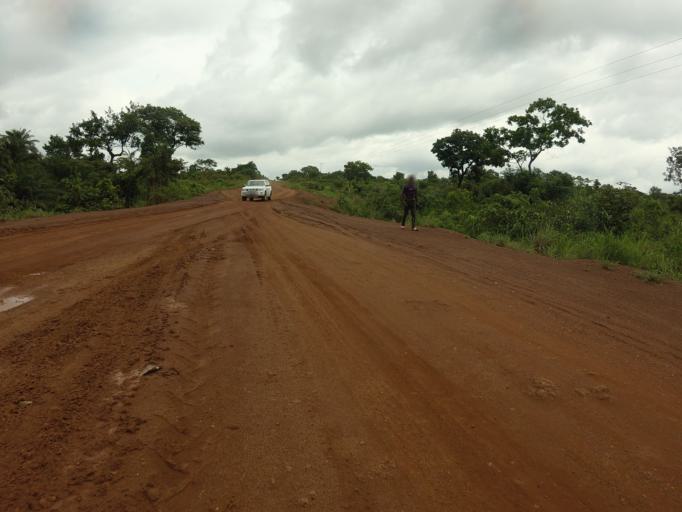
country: GH
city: Kpandae
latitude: 8.3163
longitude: 0.4782
